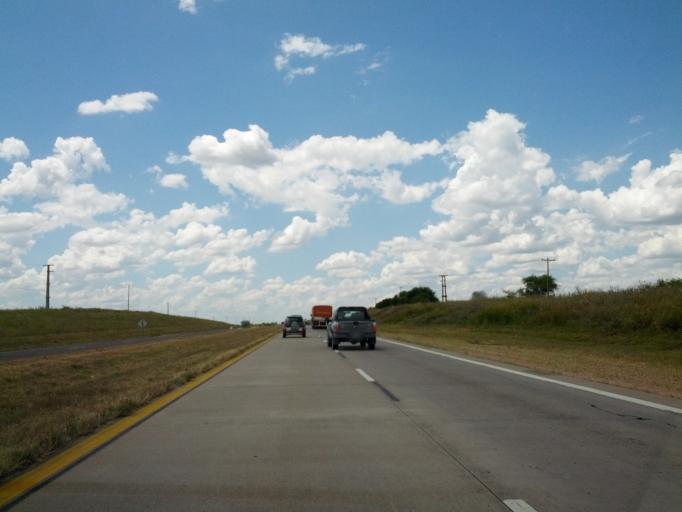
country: AR
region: Entre Rios
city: Gualeguaychu
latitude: -32.9144
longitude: -58.5628
